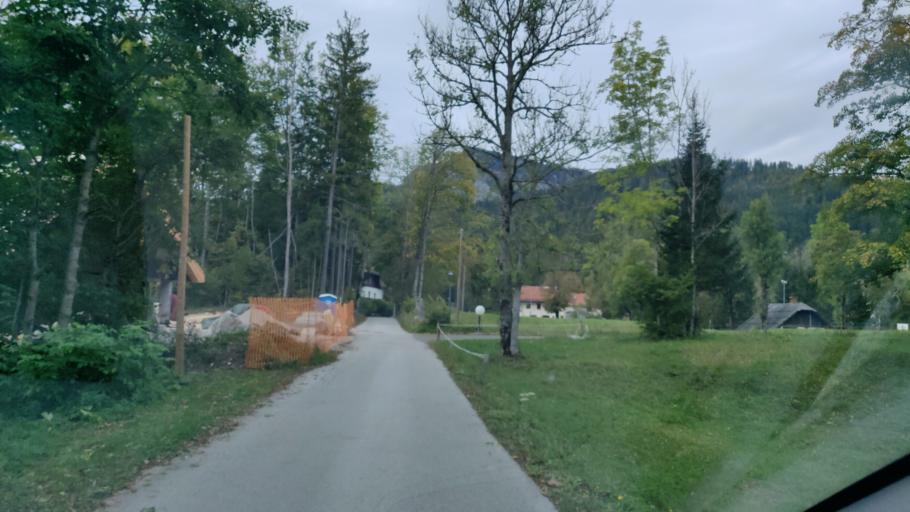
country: SI
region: Jezersko
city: Zgornje Jezersko
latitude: 46.3921
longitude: 14.5015
